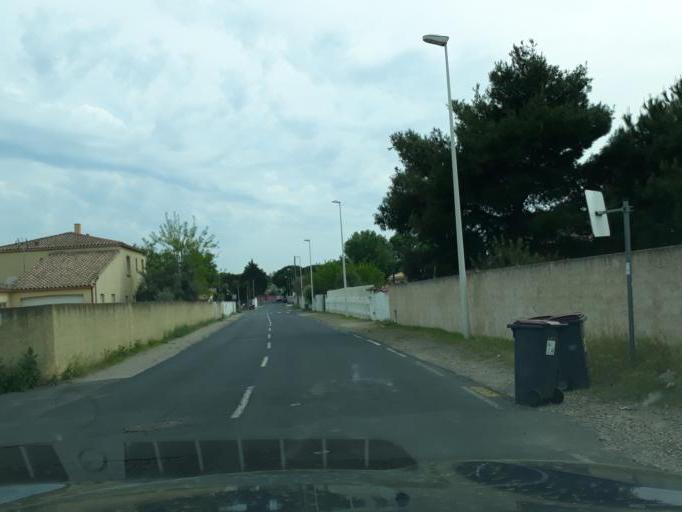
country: FR
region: Languedoc-Roussillon
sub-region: Departement de l'Herault
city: Agde
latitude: 43.2830
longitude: 3.4690
